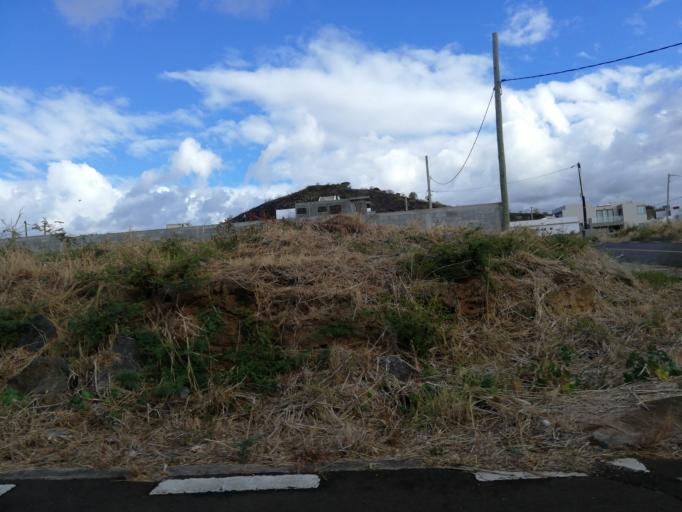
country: MU
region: Black River
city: Petite Riviere
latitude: -20.2003
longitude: 57.4632
